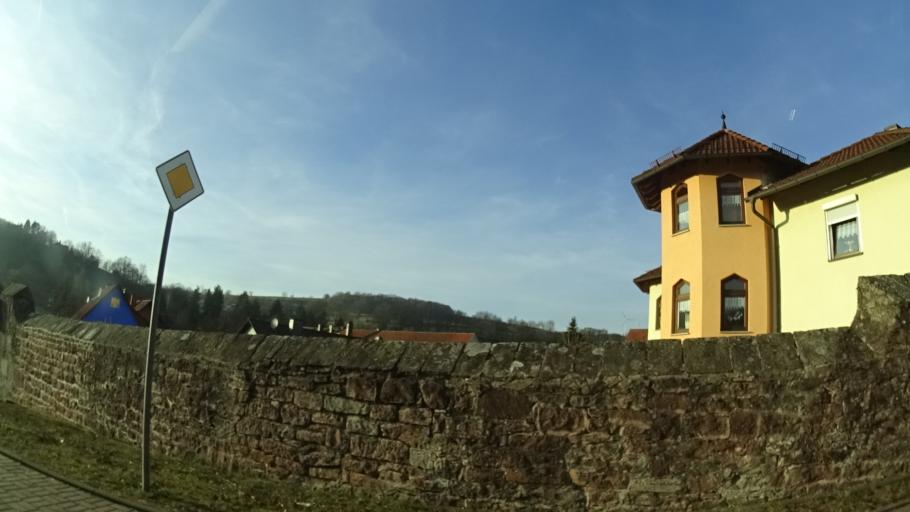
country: DE
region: Bavaria
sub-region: Regierungsbezirk Unterfranken
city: Zeitlofs
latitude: 50.2999
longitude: 9.6602
